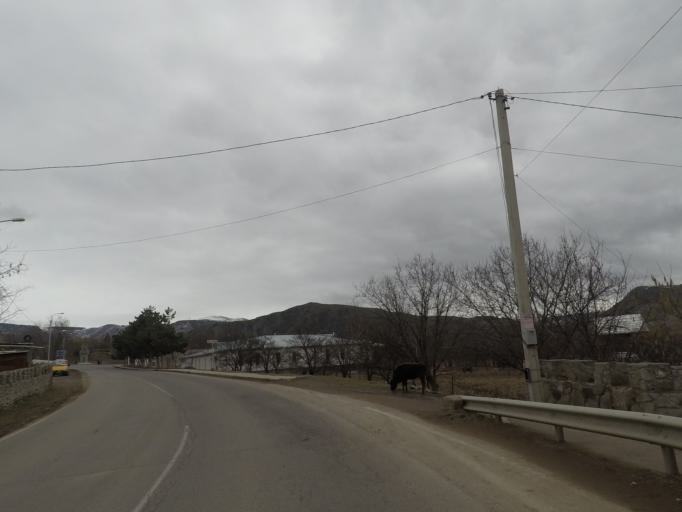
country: GE
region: Samtskhe-Javakheti
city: Aspindza
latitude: 41.5742
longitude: 43.2466
